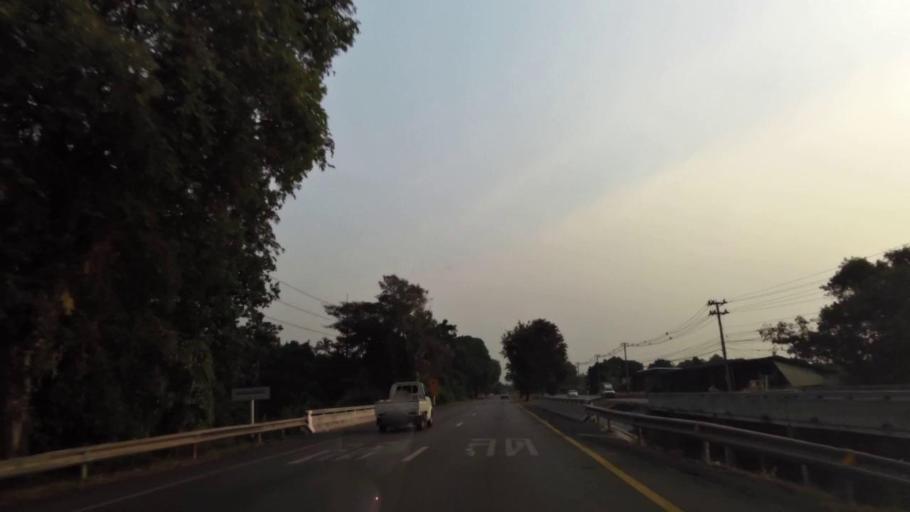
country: TH
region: Chanthaburi
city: Khlung
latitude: 12.4911
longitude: 102.1739
